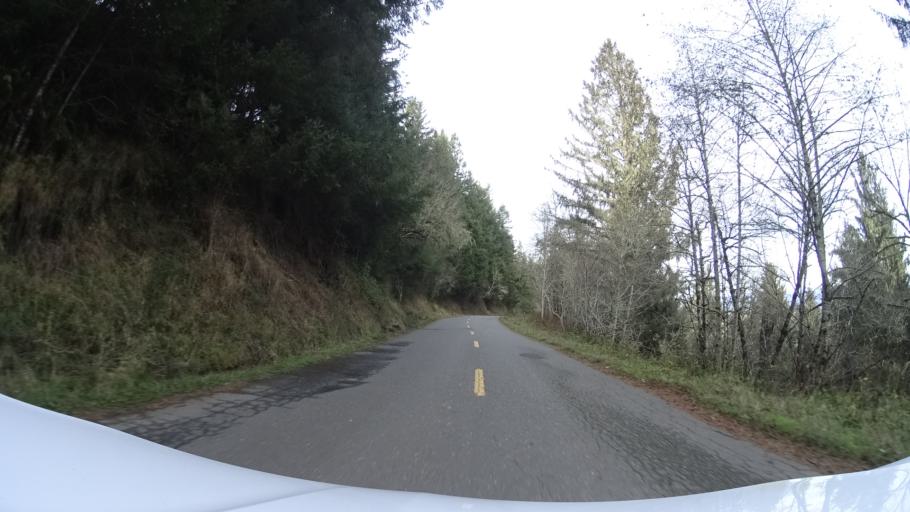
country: US
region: California
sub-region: Humboldt County
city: Ferndale
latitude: 40.5493
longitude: -124.2749
